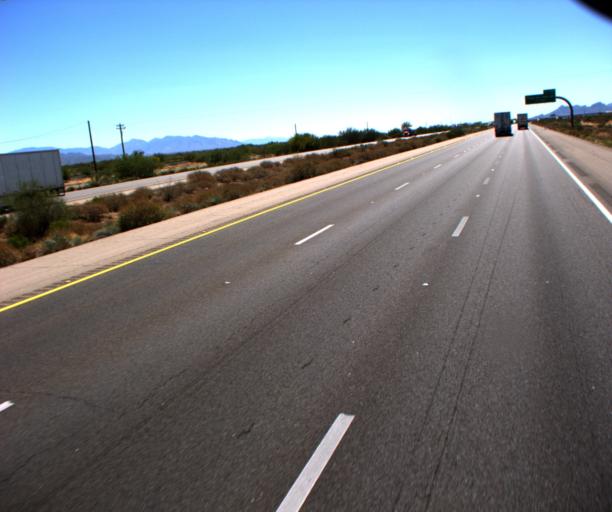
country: US
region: Arizona
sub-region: Pima County
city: Avra Valley
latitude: 32.5178
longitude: -111.2767
